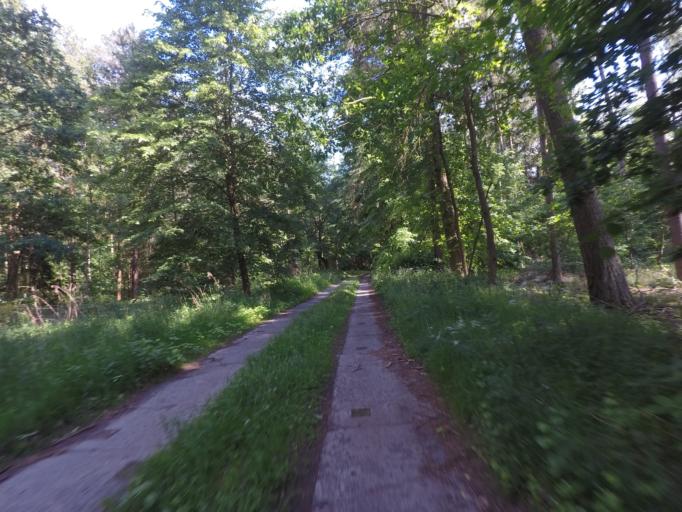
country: DE
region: Brandenburg
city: Britz
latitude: 52.8659
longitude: 13.7836
